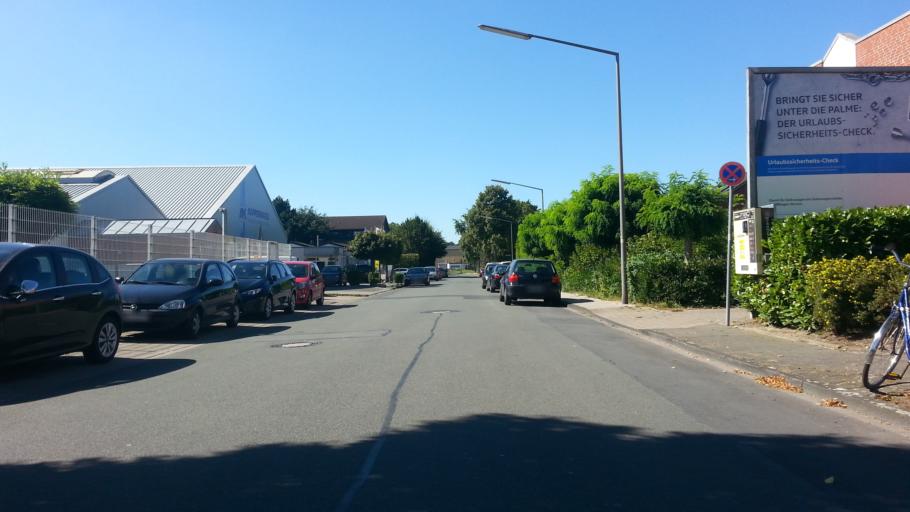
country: DE
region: North Rhine-Westphalia
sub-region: Regierungsbezirk Munster
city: Muenster
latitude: 51.9515
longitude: 7.5531
